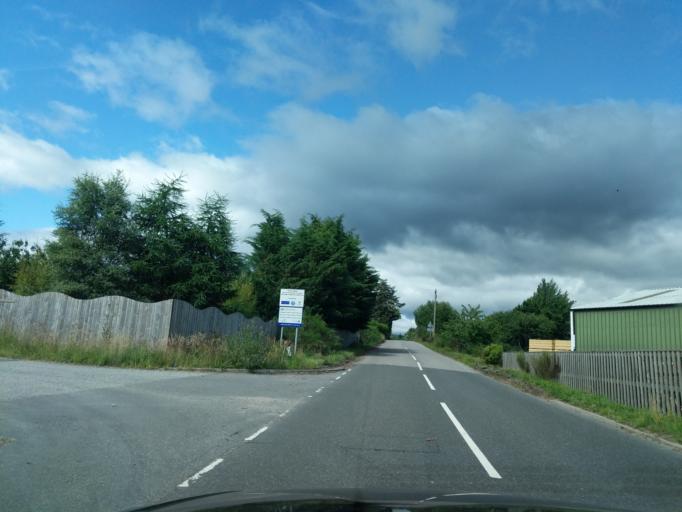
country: GB
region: Scotland
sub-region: Aberdeenshire
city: Aboyne
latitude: 57.0698
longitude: -2.8534
